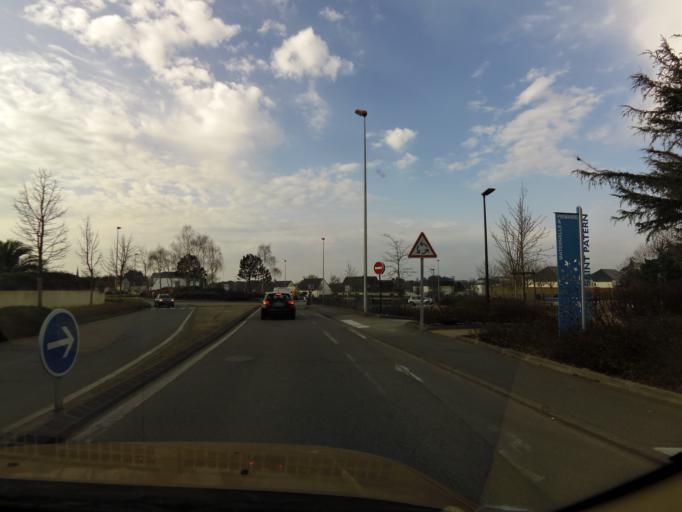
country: FR
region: Brittany
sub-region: Departement du Morbihan
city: Vannes
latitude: 47.6539
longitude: -2.7406
